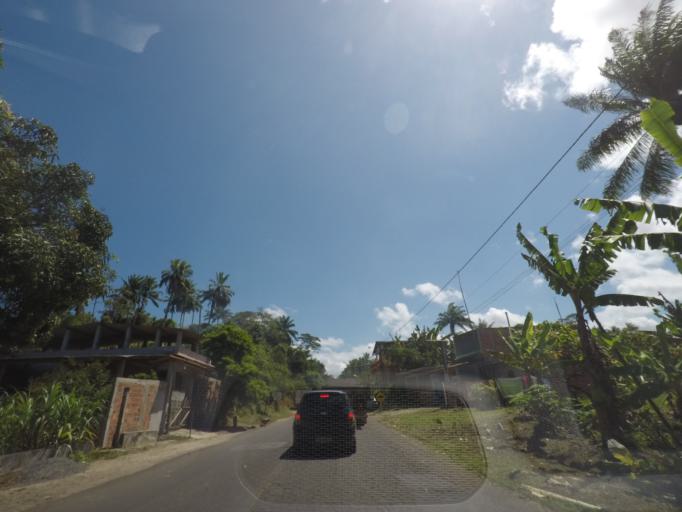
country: BR
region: Bahia
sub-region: Valenca
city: Valenca
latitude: -13.4495
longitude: -39.0856
